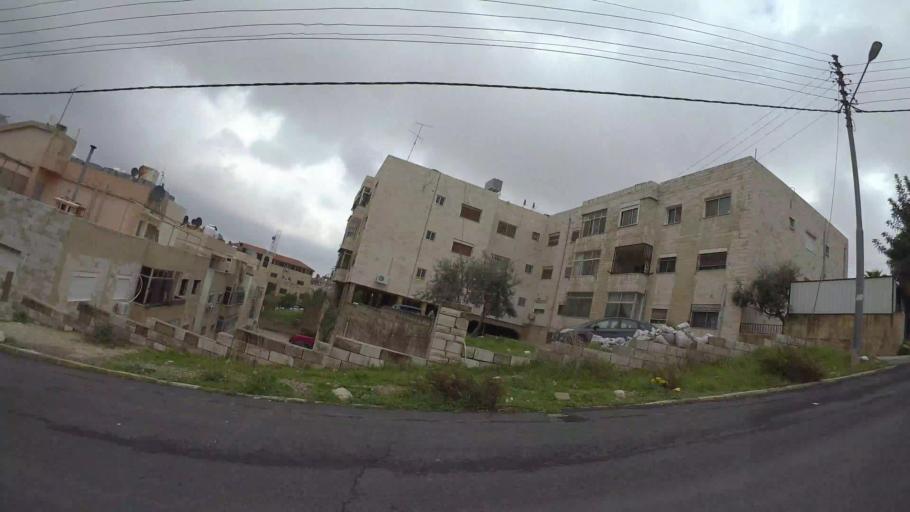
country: JO
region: Amman
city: Al Bunayyat ash Shamaliyah
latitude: 31.9423
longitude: 35.8909
